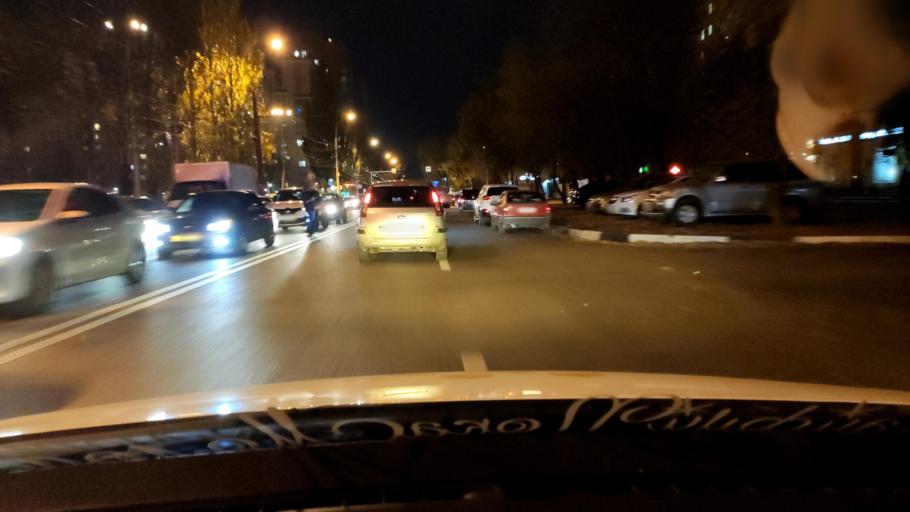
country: RU
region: Voronezj
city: Voronezh
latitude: 51.7022
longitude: 39.1960
